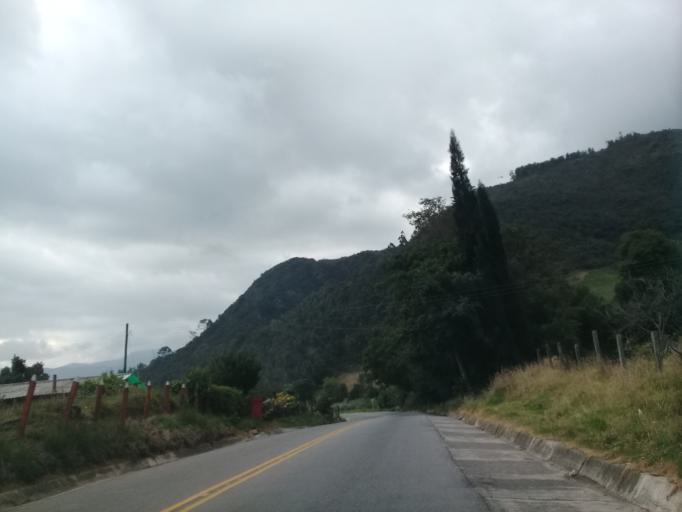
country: CO
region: Cundinamarca
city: Zipaquira
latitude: 5.0298
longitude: -74.0279
